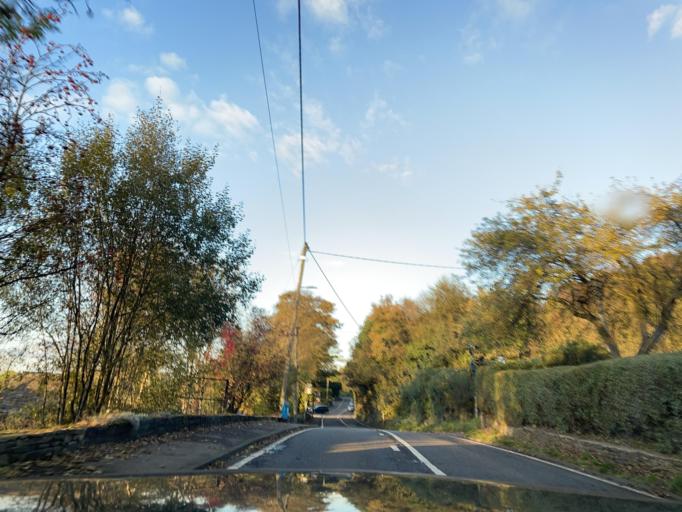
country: GB
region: England
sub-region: Borough of Stockport
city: Marple
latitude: 53.4207
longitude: -2.0307
